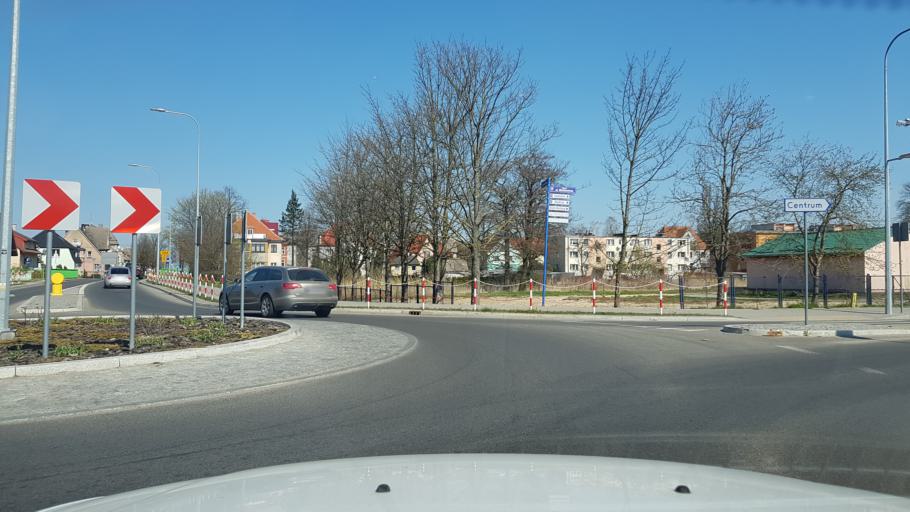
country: PL
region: West Pomeranian Voivodeship
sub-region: Powiat slawienski
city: Slawno
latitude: 54.3636
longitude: 16.6743
